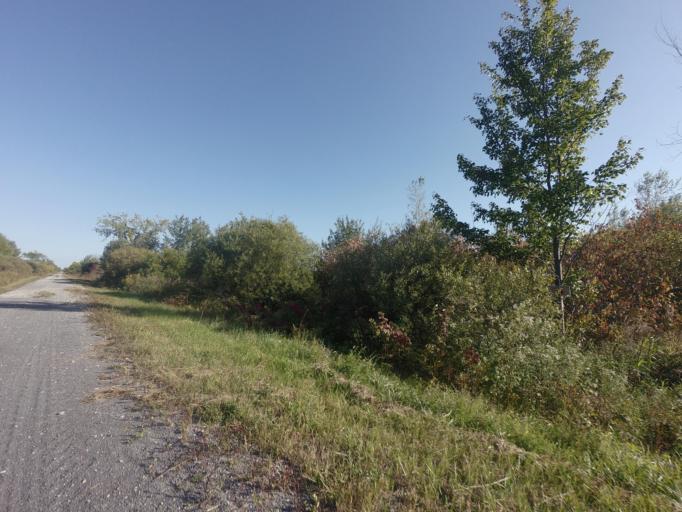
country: CA
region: Ontario
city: Hawkesbury
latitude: 45.5347
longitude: -74.5926
